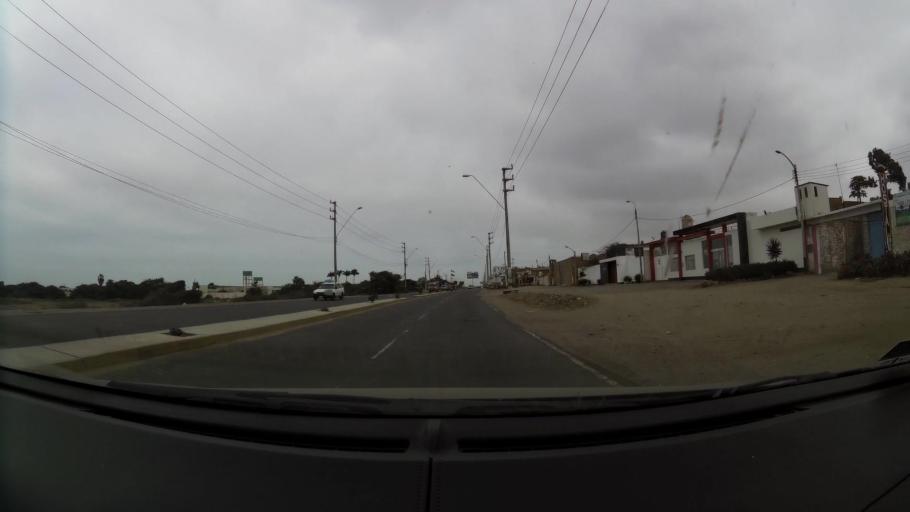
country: PE
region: La Libertad
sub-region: Provincia de Trujillo
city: Huanchaco
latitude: -8.0922
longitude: -79.0813
